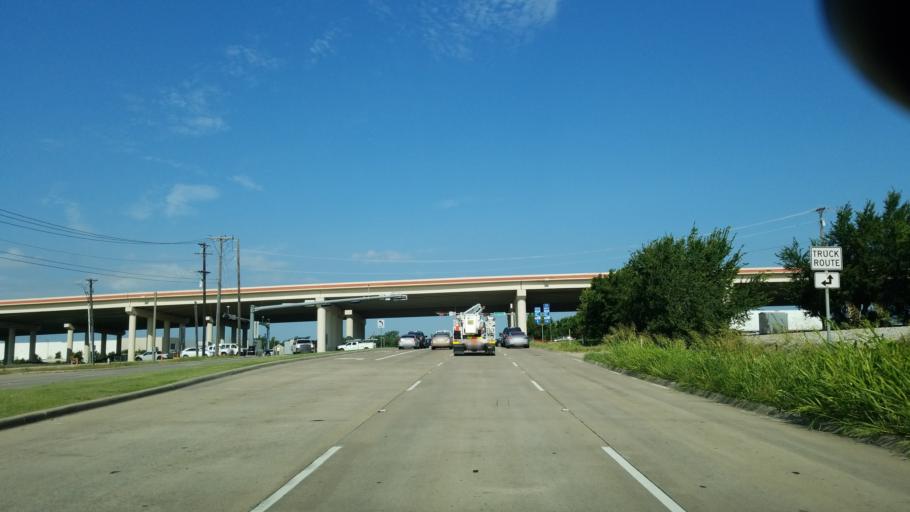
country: US
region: Texas
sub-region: Dallas County
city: Carrollton
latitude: 32.9520
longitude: -96.9239
